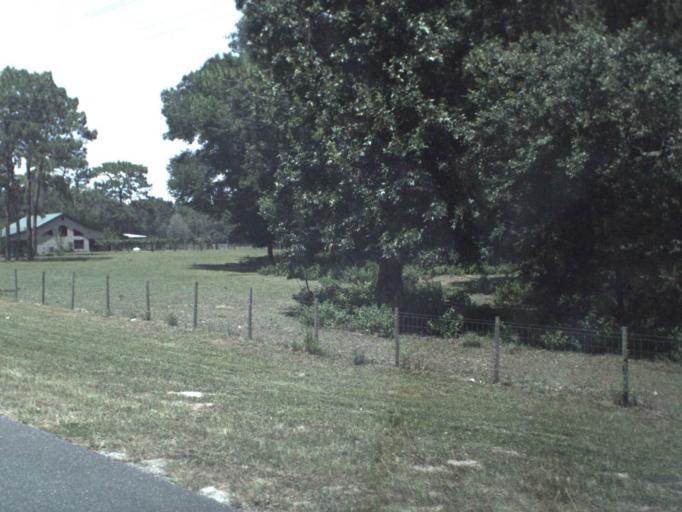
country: US
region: Florida
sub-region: Lafayette County
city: Mayo
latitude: 29.8792
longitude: -82.9561
